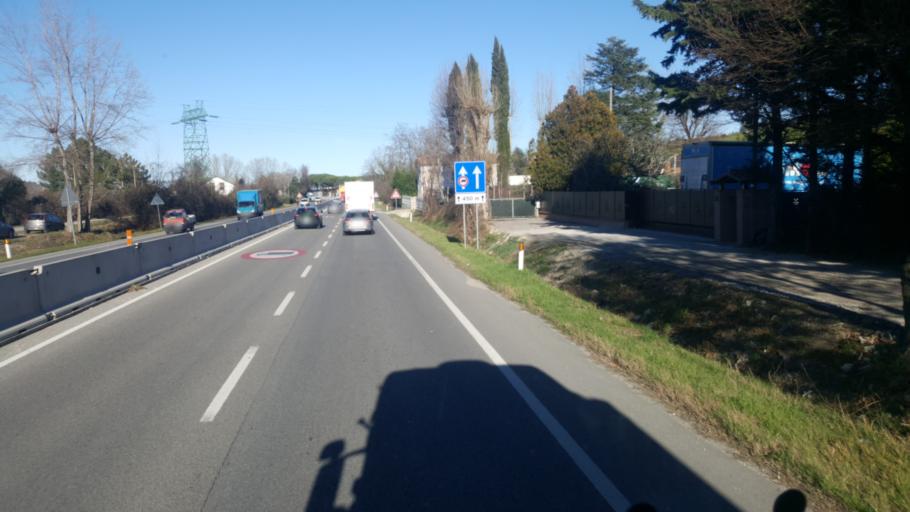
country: IT
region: Emilia-Romagna
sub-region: Provincia di Rimini
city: Cerasolo
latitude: 43.9962
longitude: 12.5396
